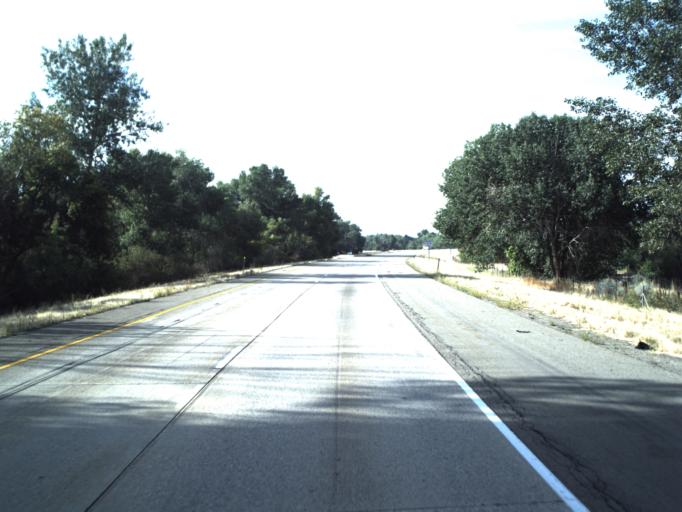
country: US
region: Utah
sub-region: Weber County
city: Riverdale
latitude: 41.1597
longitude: -111.9932
